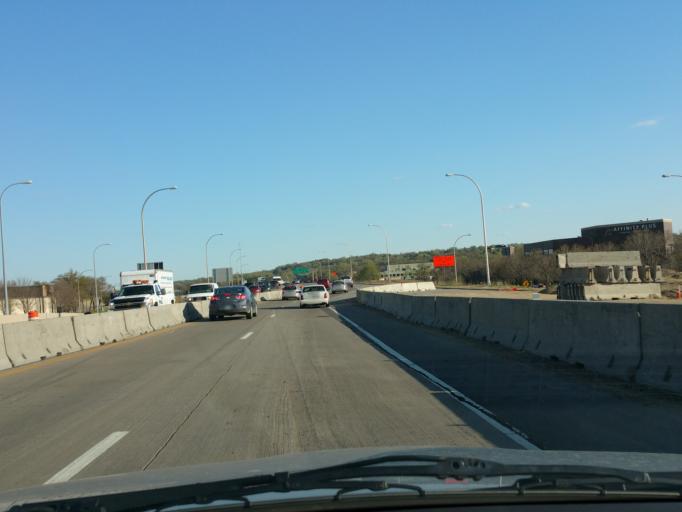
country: US
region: Minnesota
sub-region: Ramsey County
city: Saint Paul
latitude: 44.9423
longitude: -93.0769
